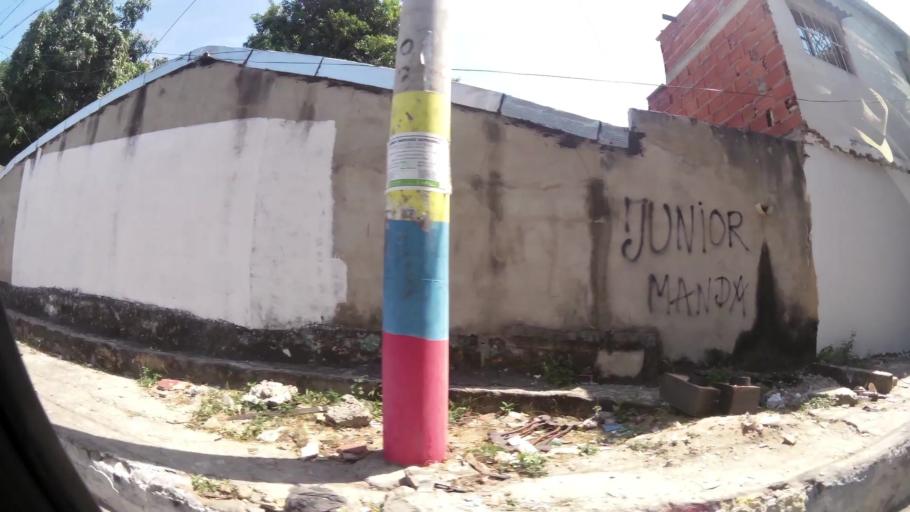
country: CO
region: Atlantico
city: Barranquilla
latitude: 10.9663
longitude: -74.8062
